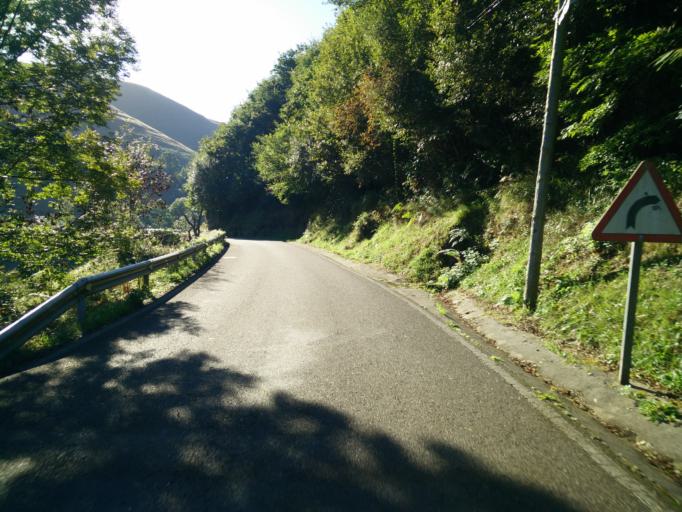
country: ES
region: Cantabria
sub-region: Provincia de Cantabria
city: San Pedro del Romeral
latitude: 43.1500
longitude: -3.8205
